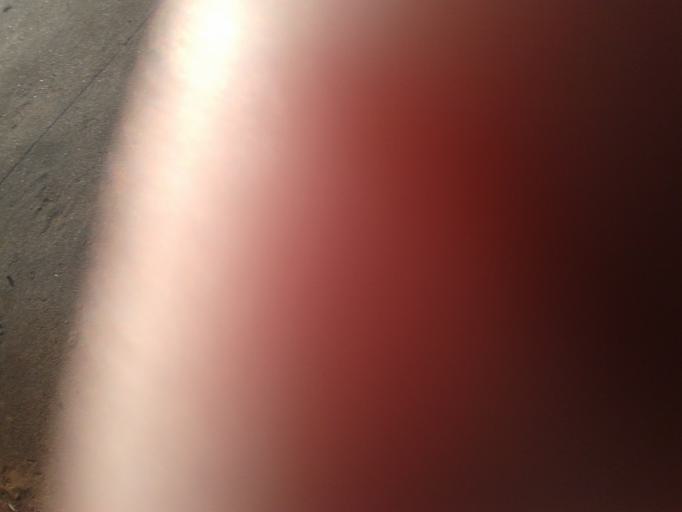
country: AR
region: Misiones
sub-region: Departamento de Capital
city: Posadas
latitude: -27.3954
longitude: -55.9636
